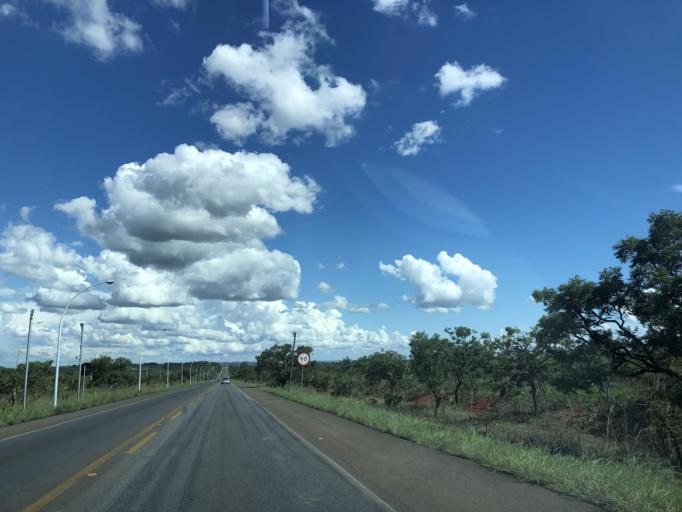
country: BR
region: Federal District
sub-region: Brasilia
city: Brasilia
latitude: -15.6722
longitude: -47.8785
